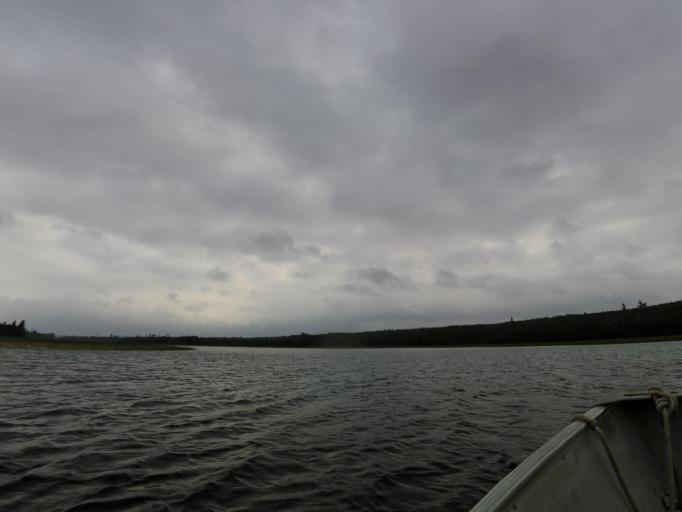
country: CA
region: Ontario
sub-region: Rainy River District
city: Atikokan
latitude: 49.5864
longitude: -91.3741
